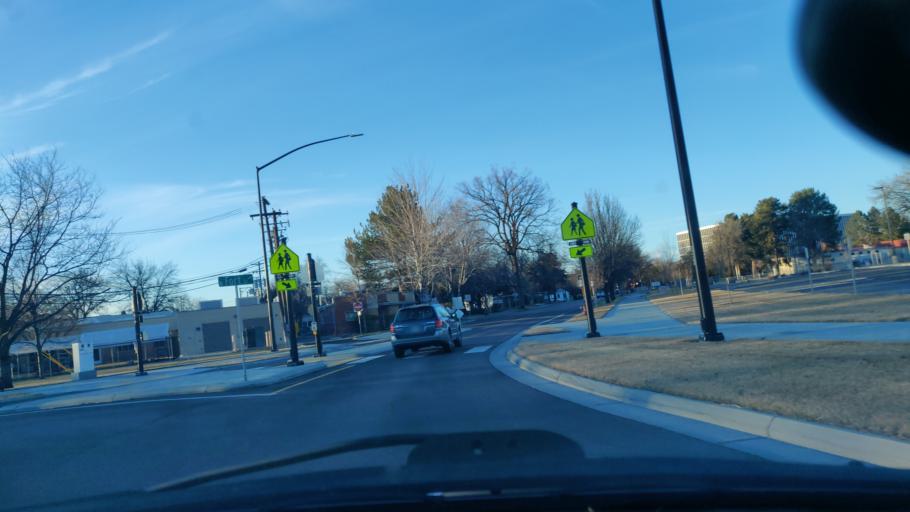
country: US
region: Idaho
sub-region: Ada County
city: Boise
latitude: 43.6166
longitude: -116.1932
